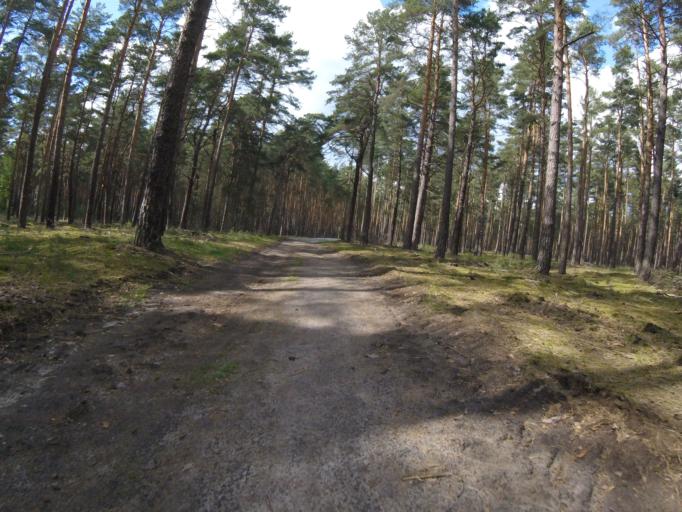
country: DE
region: Brandenburg
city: Schwerin
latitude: 52.1923
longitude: 13.5953
